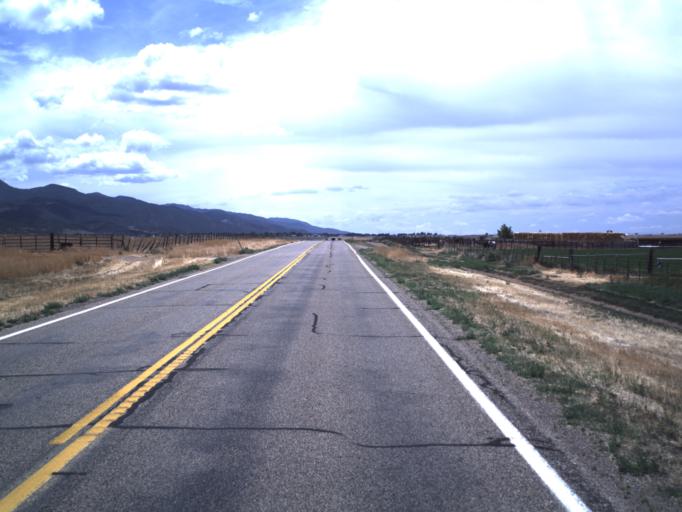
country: US
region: Utah
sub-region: Iron County
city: Parowan
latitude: 37.8756
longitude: -112.7861
